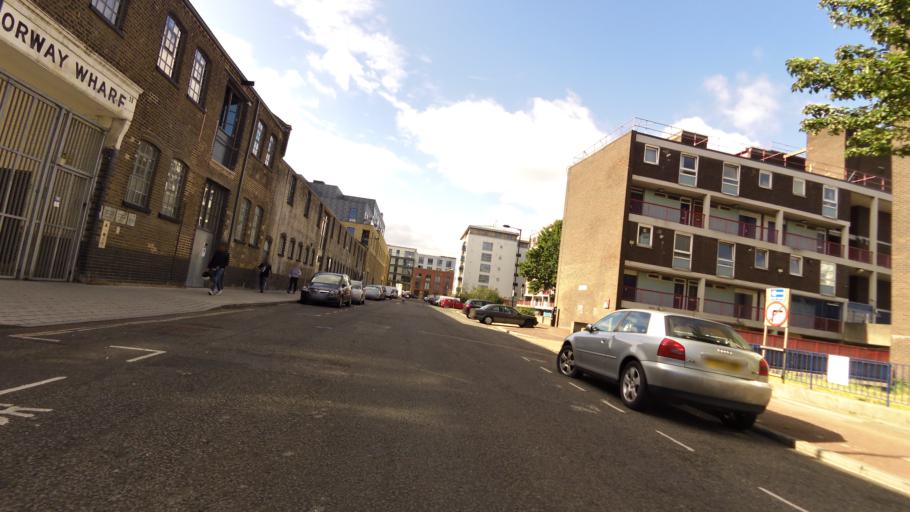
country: GB
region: England
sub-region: Greater London
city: Bethnal Green
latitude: 51.5385
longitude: -0.0789
